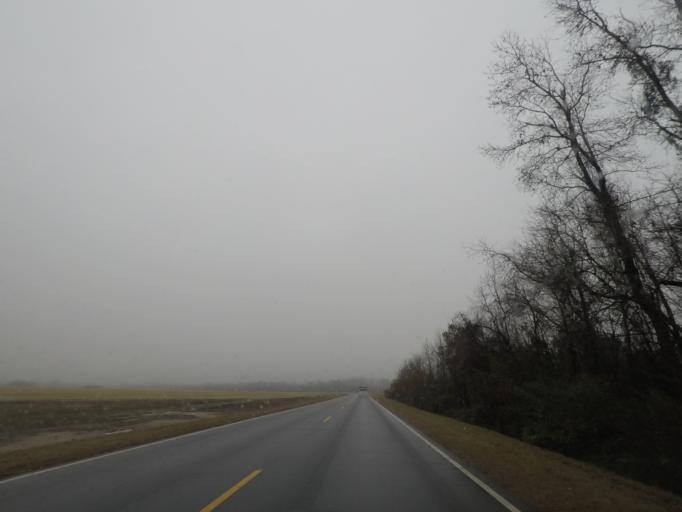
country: US
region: North Carolina
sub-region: Scotland County
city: Laurinburg
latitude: 34.7836
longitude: -79.4308
